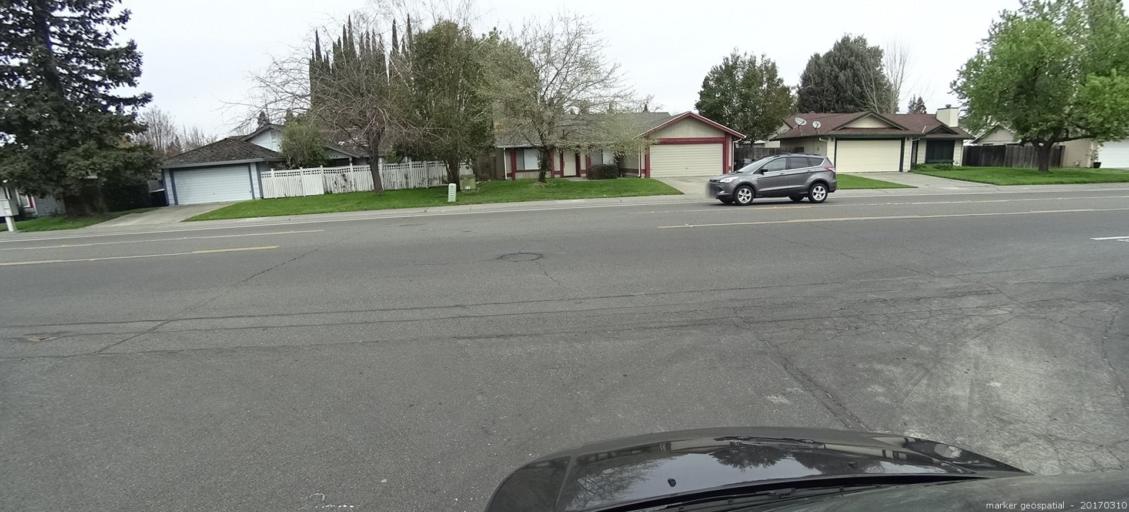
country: US
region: California
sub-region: Sacramento County
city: Parkway
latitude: 38.4876
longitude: -121.5308
